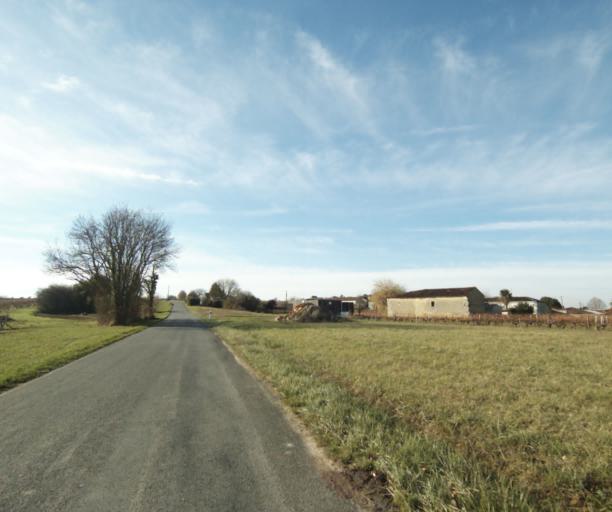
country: FR
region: Poitou-Charentes
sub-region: Departement de la Charente-Maritime
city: Burie
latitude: 45.7773
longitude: -0.4049
